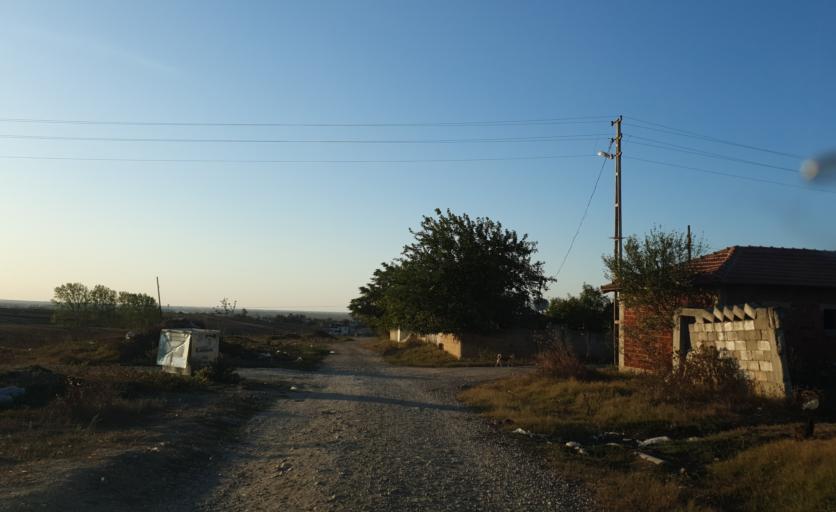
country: TR
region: Tekirdag
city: Beyazkoy
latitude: 41.3300
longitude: 27.7445
